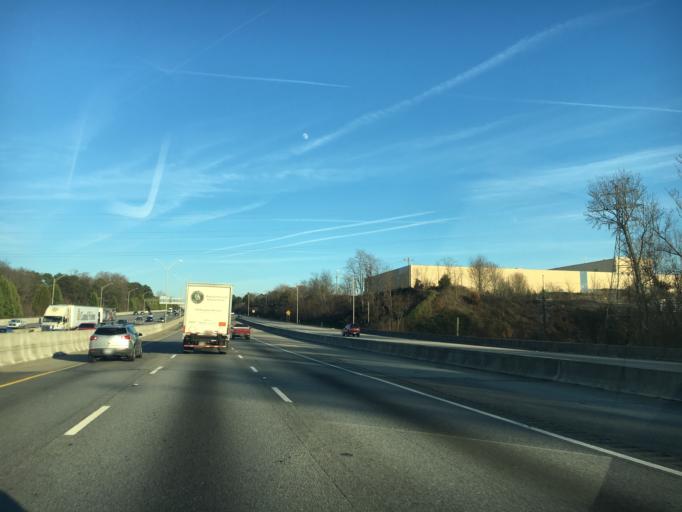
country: US
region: South Carolina
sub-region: Greenville County
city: Gantt
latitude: 34.8009
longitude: -82.3655
